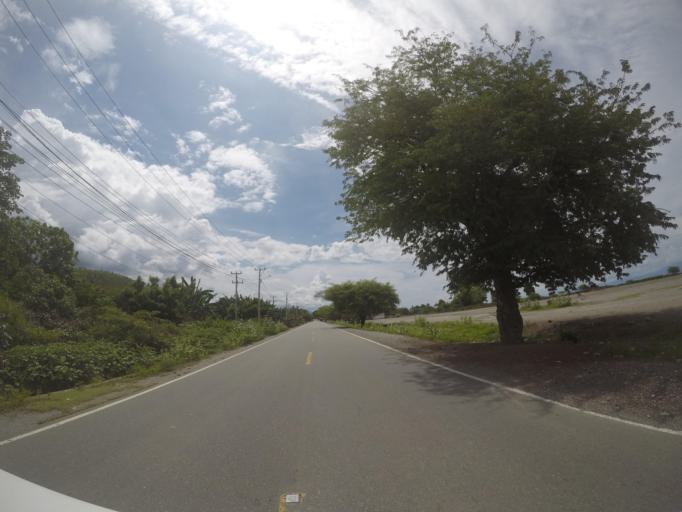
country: TL
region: Liquica
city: Liquica
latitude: -8.5788
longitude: 125.3643
